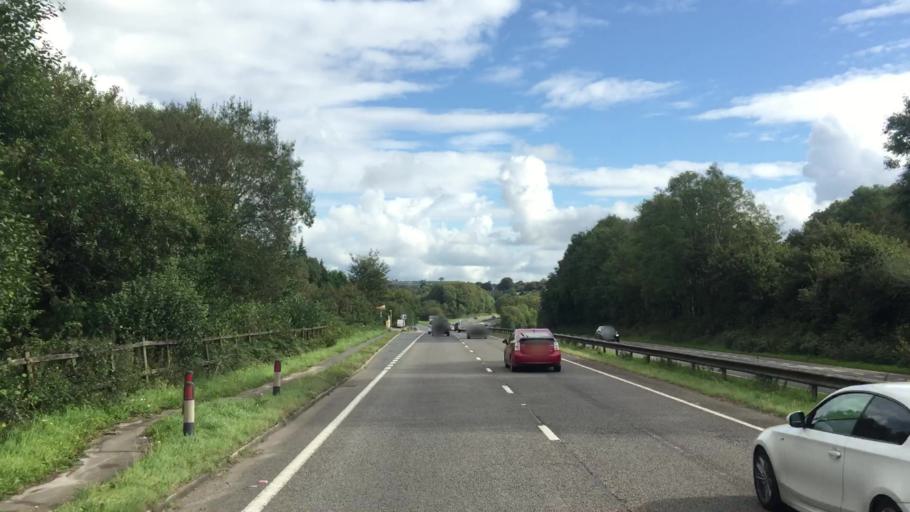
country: GB
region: England
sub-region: Devon
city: South Brent
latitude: 50.4136
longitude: -3.8447
